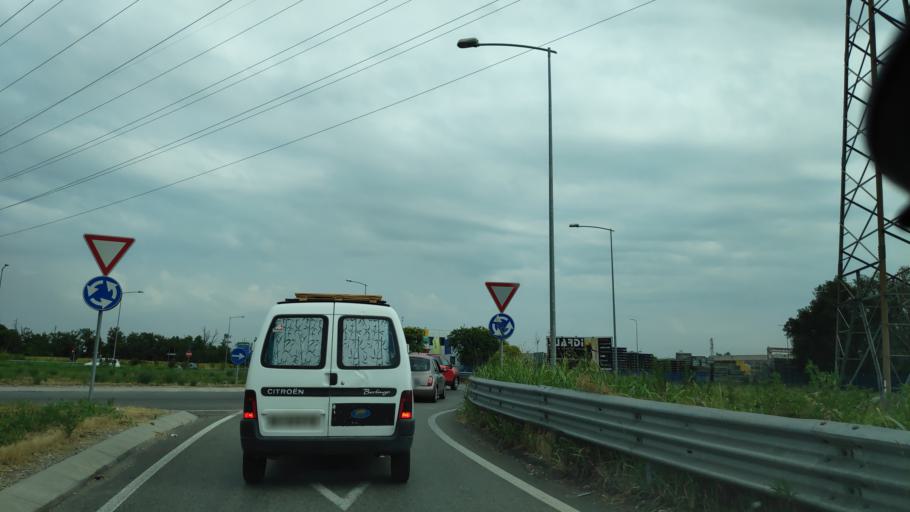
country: IT
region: Lombardy
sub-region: Citta metropolitana di Milano
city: Colturano
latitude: 45.3707
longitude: 9.3360
